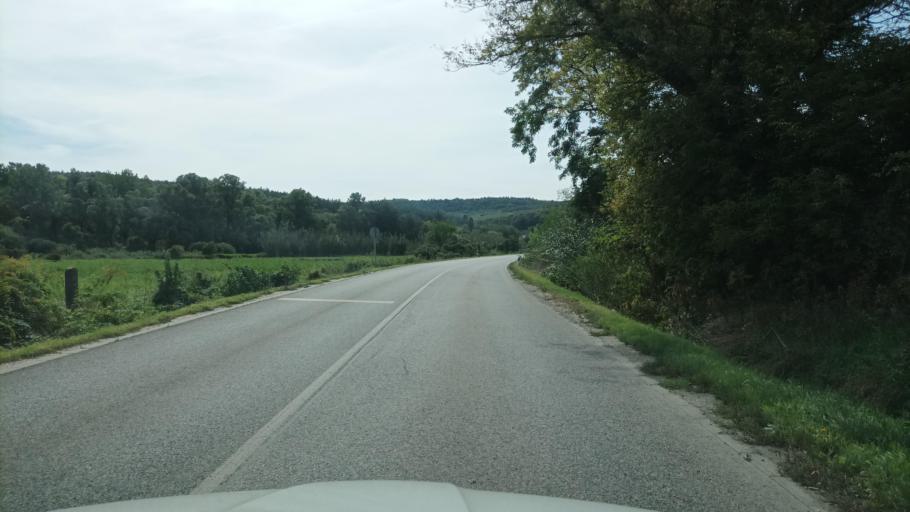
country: HU
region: Pest
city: Pecel
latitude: 47.4983
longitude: 19.3715
